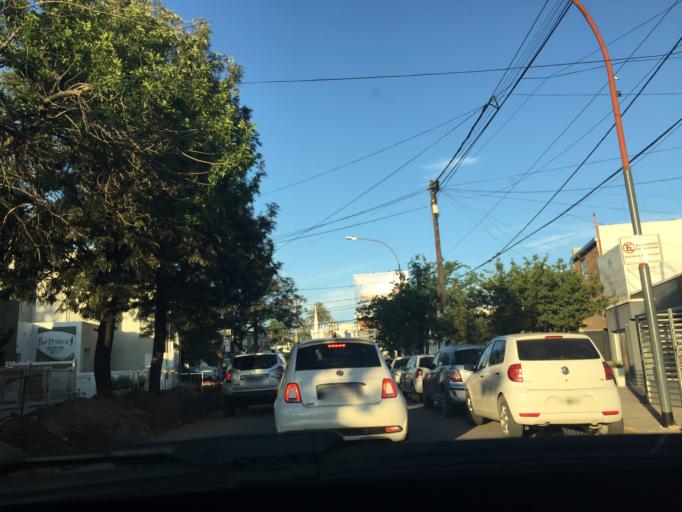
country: AR
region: Cordoba
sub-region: Departamento de Capital
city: Cordoba
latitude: -31.3677
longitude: -64.2346
